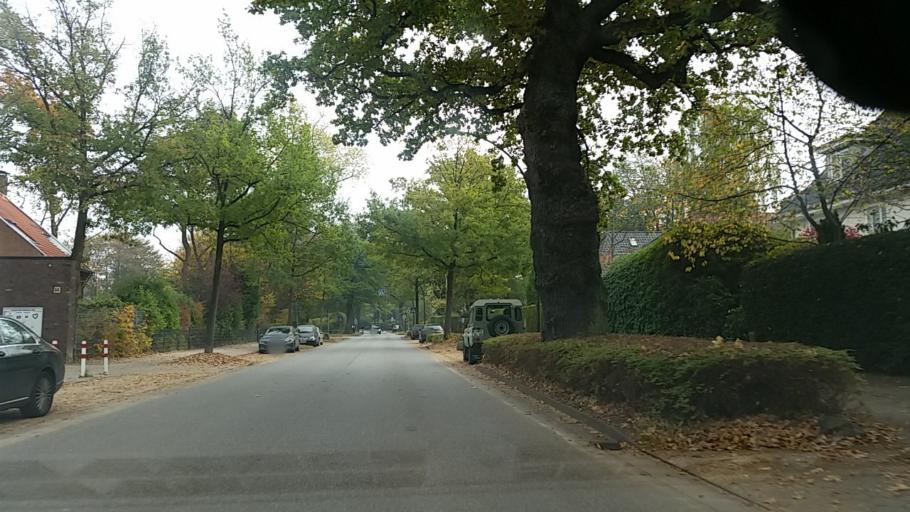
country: DE
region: Hamburg
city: Altona
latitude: 53.5527
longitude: 9.8838
